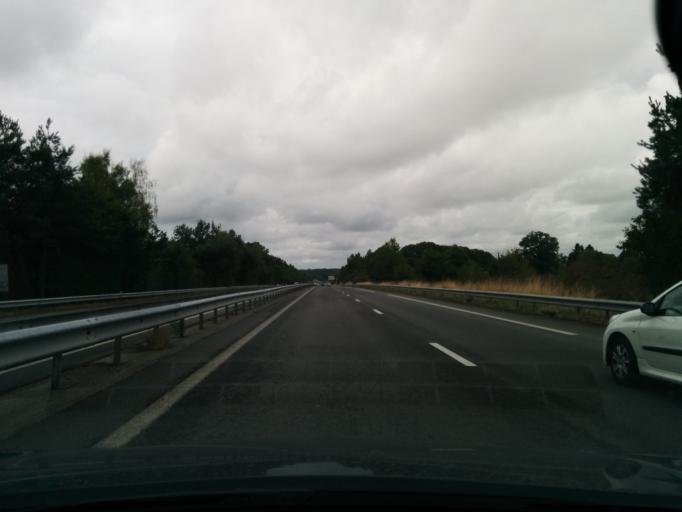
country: FR
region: Limousin
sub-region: Departement de la Haute-Vienne
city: Saint-Germain-les-Belles
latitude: 45.5792
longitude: 1.4809
